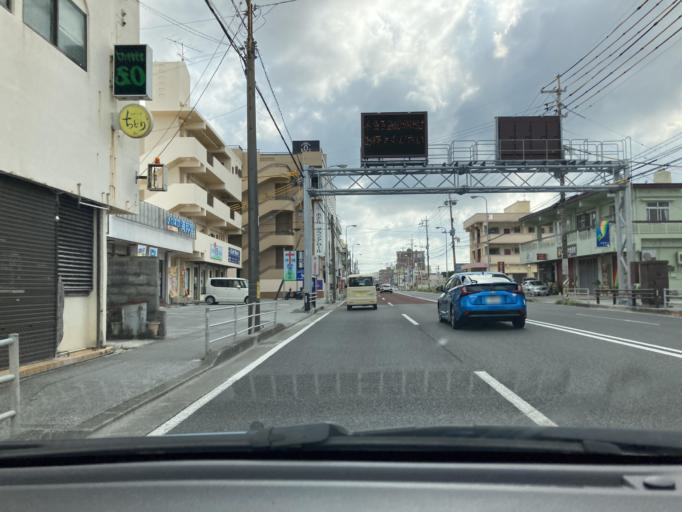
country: JP
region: Okinawa
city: Ginowan
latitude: 26.2104
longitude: 127.7592
